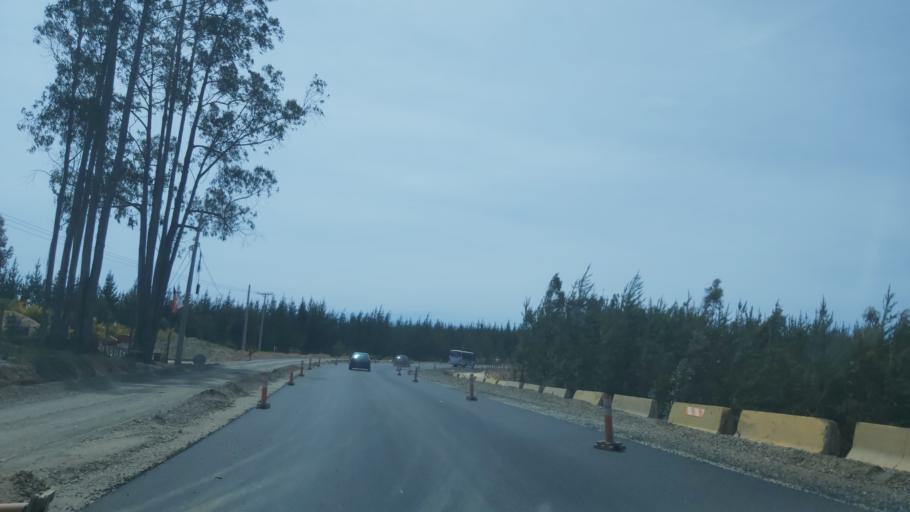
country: CL
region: Maule
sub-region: Provincia de Talca
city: Constitucion
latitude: -35.3842
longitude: -72.4201
